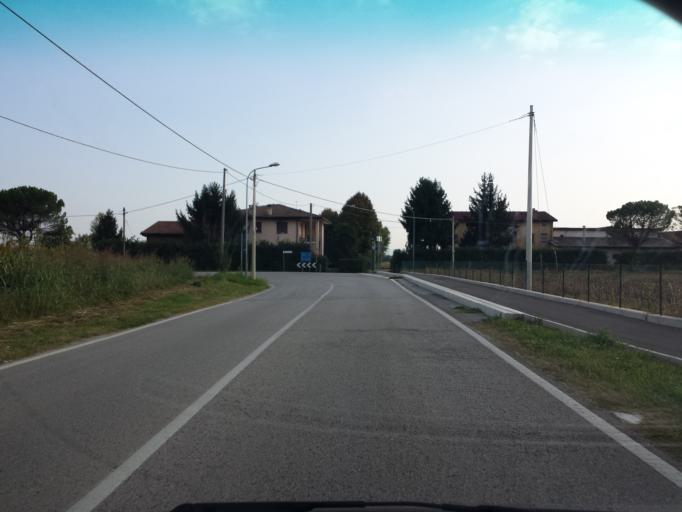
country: IT
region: Veneto
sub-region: Provincia di Vicenza
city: Dueville
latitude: 45.6204
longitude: 11.5536
